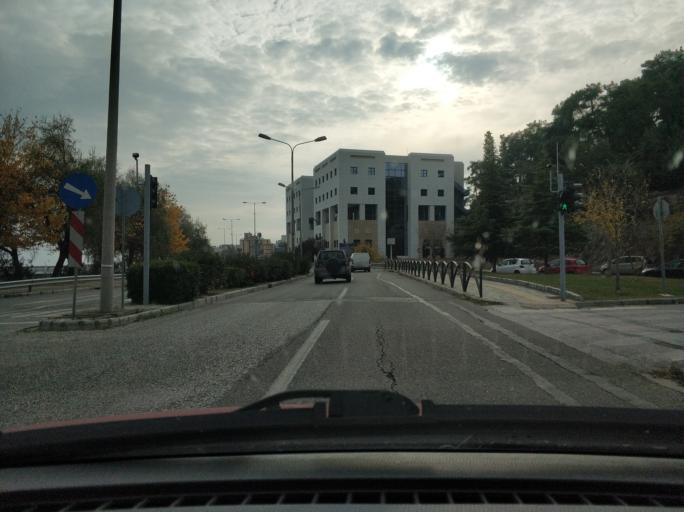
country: GR
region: East Macedonia and Thrace
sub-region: Nomos Kavalas
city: Kavala
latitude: 40.9312
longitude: 24.3920
